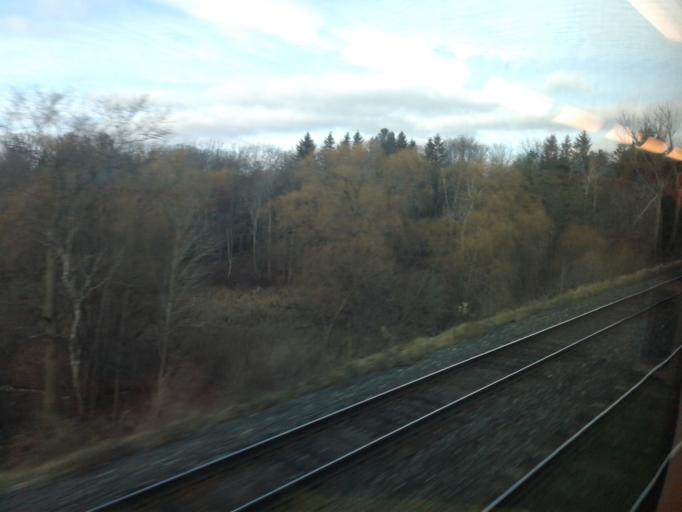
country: CA
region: Ontario
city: Mississauga
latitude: 43.5367
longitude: -79.6083
